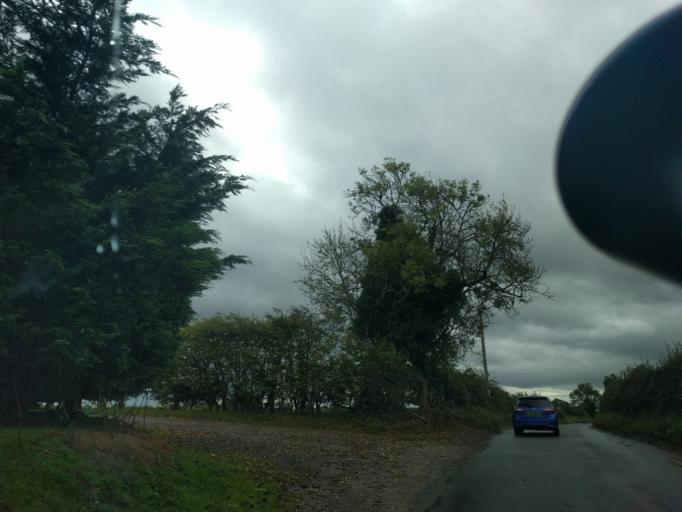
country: GB
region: England
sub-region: North Yorkshire
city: Bedale
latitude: 54.3174
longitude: -1.5635
